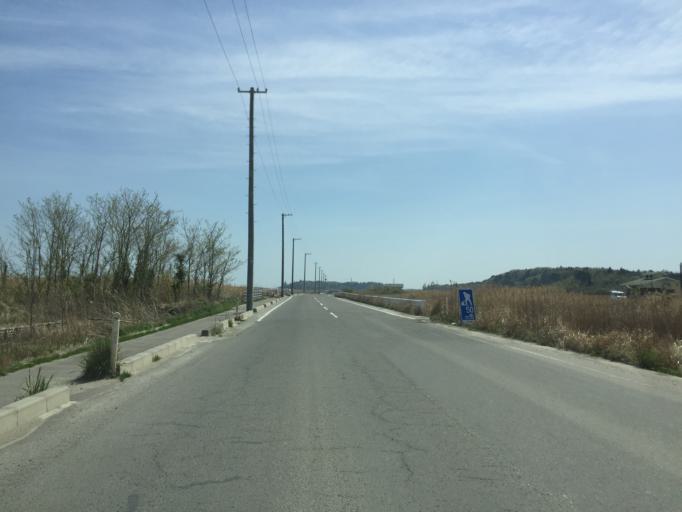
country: JP
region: Miyagi
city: Watari
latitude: 37.9151
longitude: 140.9176
